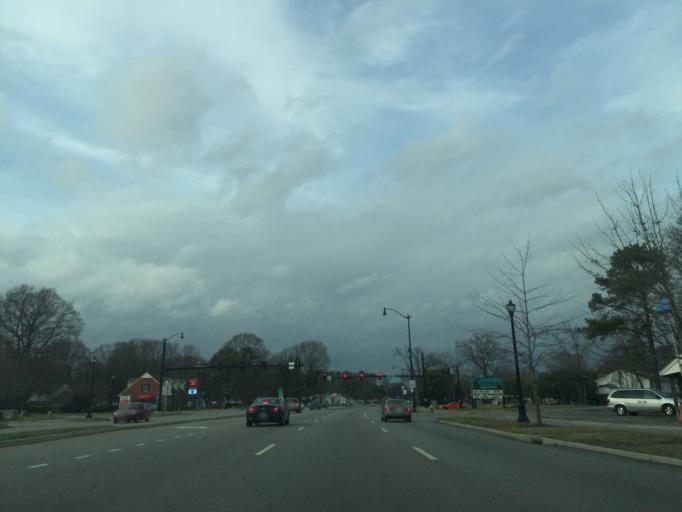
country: US
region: Virginia
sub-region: City of Newport News
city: Newport News
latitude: 37.0793
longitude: -76.4964
